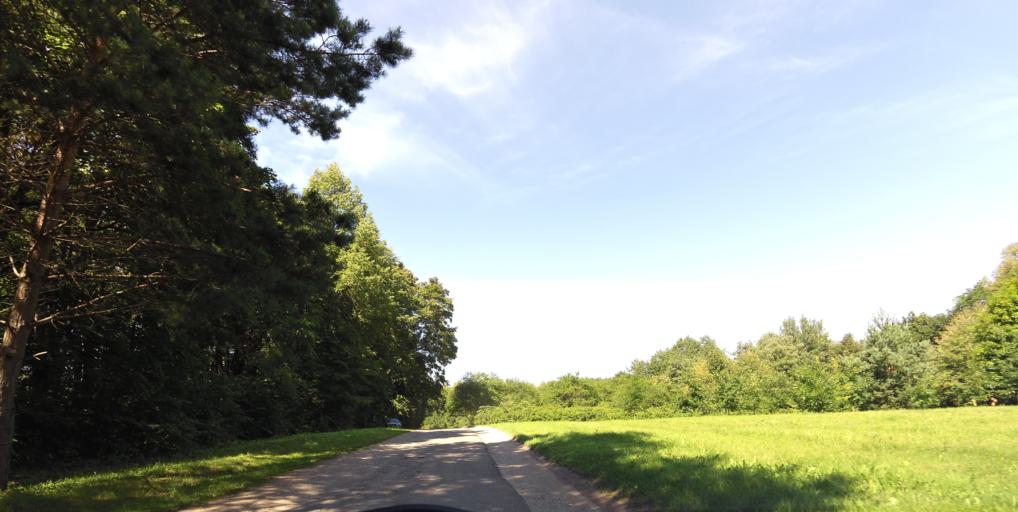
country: LT
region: Vilnius County
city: Rasos
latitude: 54.6878
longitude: 25.3632
